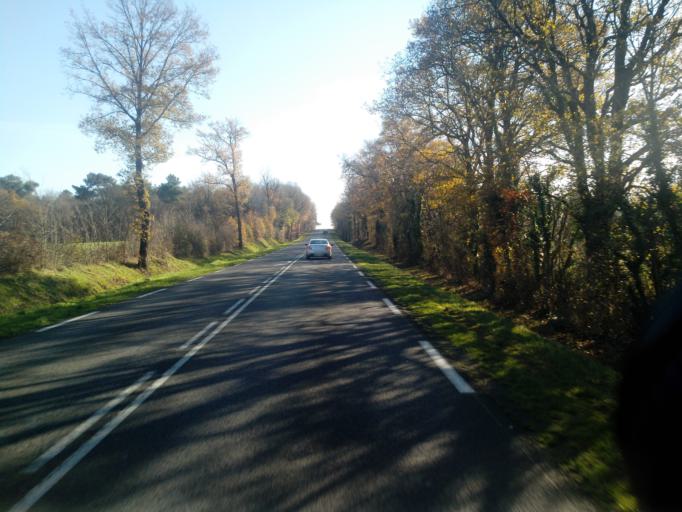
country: FR
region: Poitou-Charentes
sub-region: Departement de la Vienne
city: Lussac-les-Chateaux
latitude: 46.3571
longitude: 0.7800
